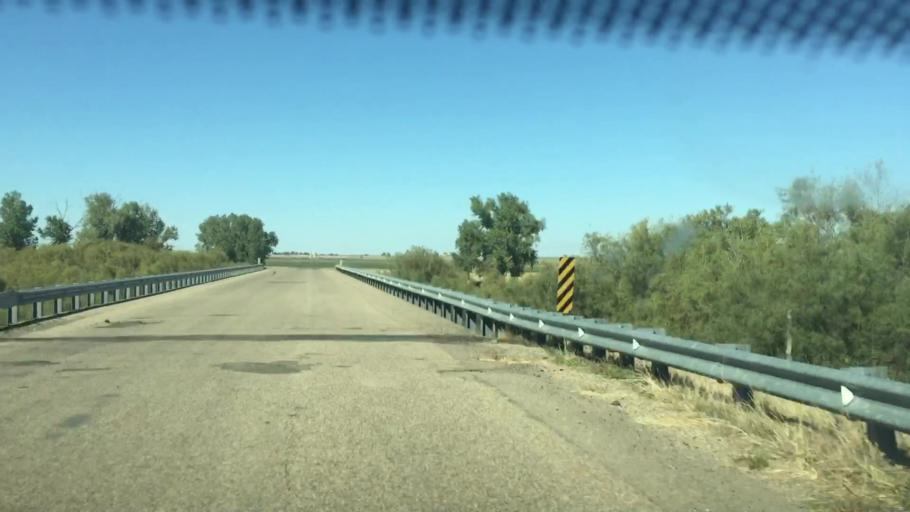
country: US
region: Colorado
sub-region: Prowers County
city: Lamar
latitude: 38.0962
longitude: -102.5195
